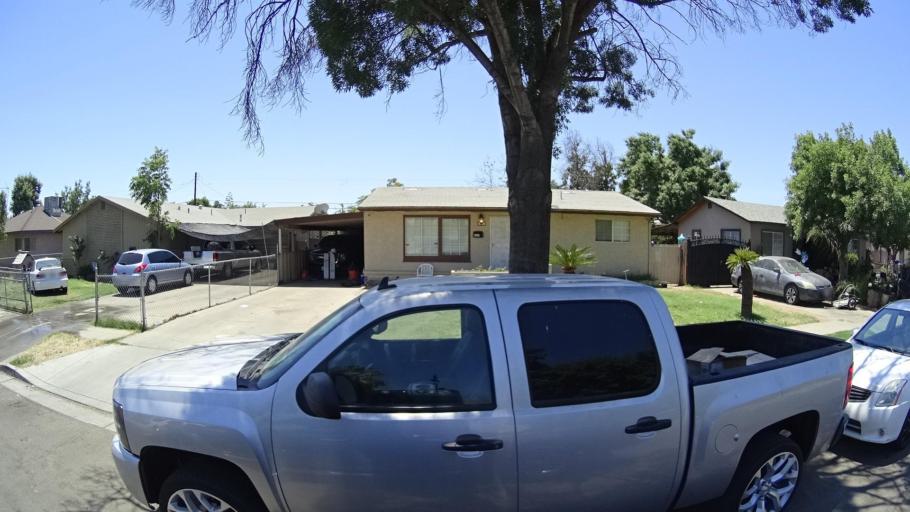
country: US
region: California
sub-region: Fresno County
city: Fresno
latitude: 36.7323
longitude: -119.7447
